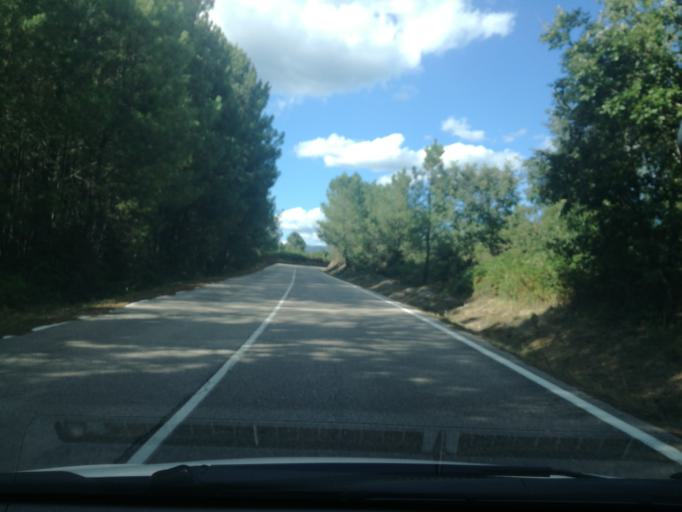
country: ES
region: Galicia
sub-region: Provincia de Ourense
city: Lobios
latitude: 41.8854
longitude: -8.0959
